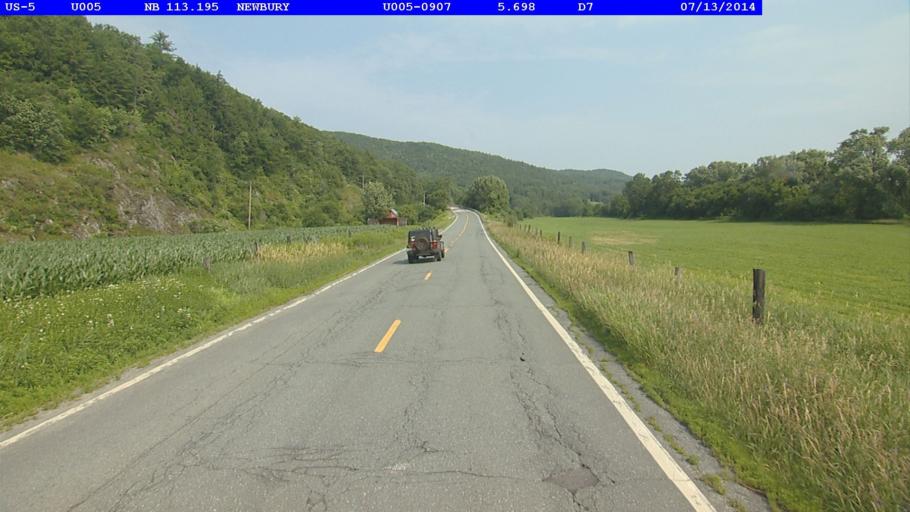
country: US
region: New Hampshire
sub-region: Grafton County
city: North Haverhill
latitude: 44.1028
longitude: -72.0536
